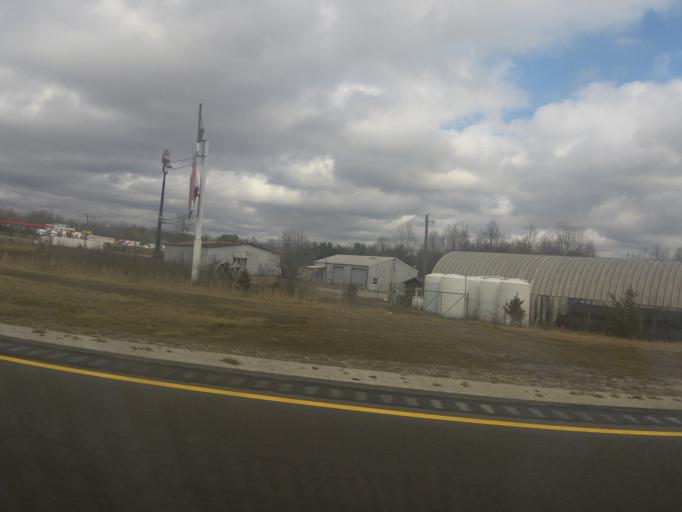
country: US
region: Tennessee
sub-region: Marion County
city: Monteagle
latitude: 35.2297
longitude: -85.8257
